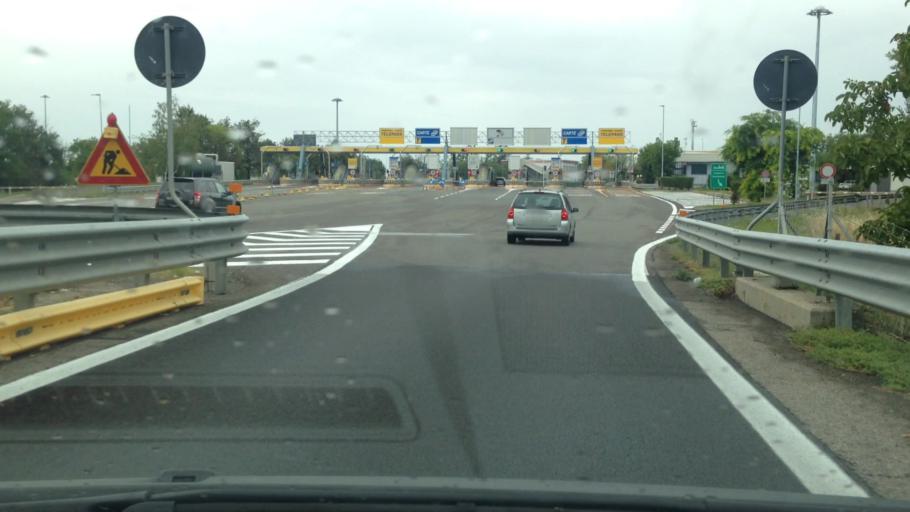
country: IT
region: Piedmont
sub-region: Provincia di Alessandria
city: Tortona
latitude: 44.9090
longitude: 8.8414
